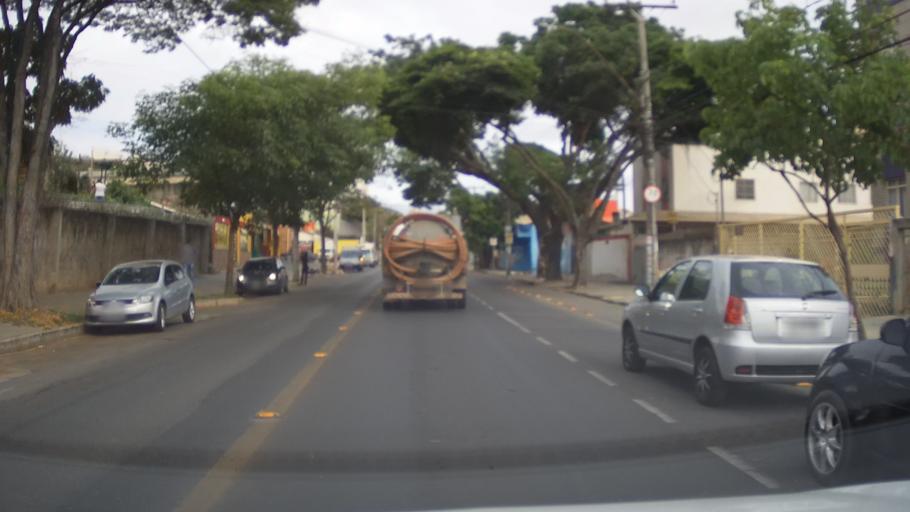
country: BR
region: Minas Gerais
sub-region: Belo Horizonte
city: Belo Horizonte
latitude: -19.8225
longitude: -43.9645
